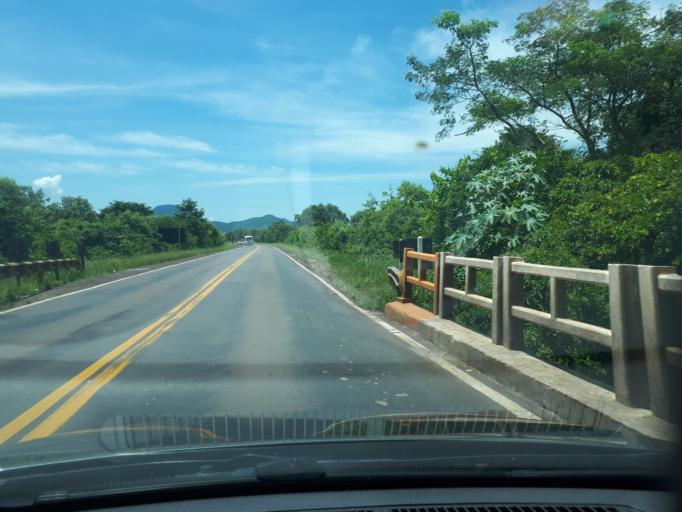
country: BR
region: Rio Grande do Sul
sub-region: Candelaria
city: Candelaria
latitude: -29.7248
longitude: -52.9247
